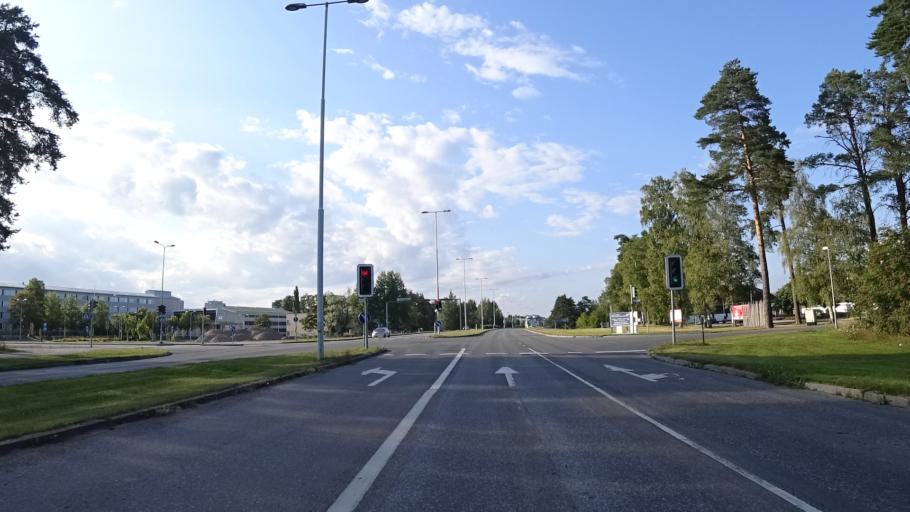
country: FI
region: South Karelia
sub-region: Imatra
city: Imatra
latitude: 61.1843
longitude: 28.7793
